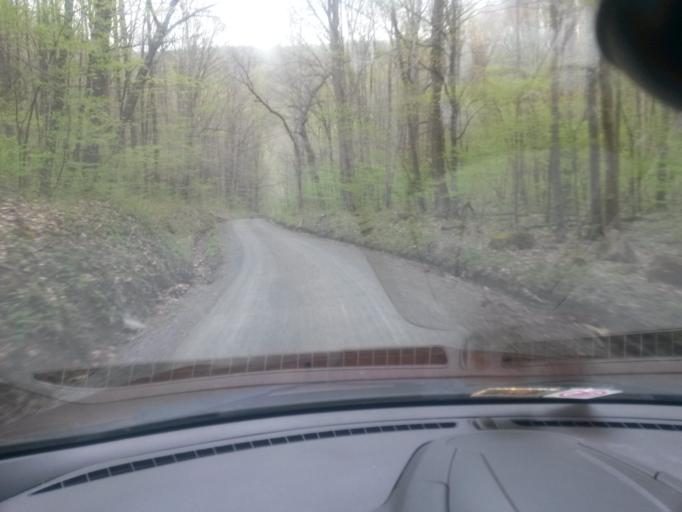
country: US
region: West Virginia
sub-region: Nicholas County
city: Richwood
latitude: 38.0545
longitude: -80.3492
